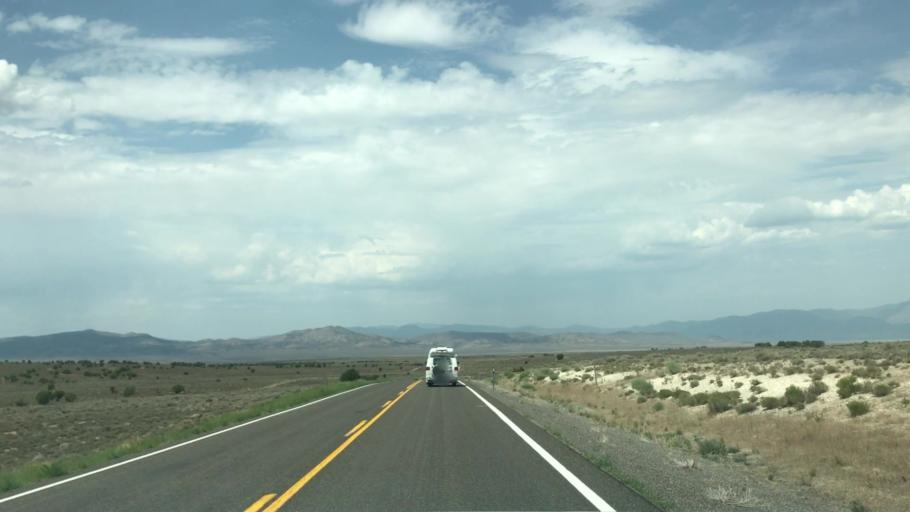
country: US
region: Nevada
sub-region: Eureka County
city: Eureka
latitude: 39.3950
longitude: -115.5309
